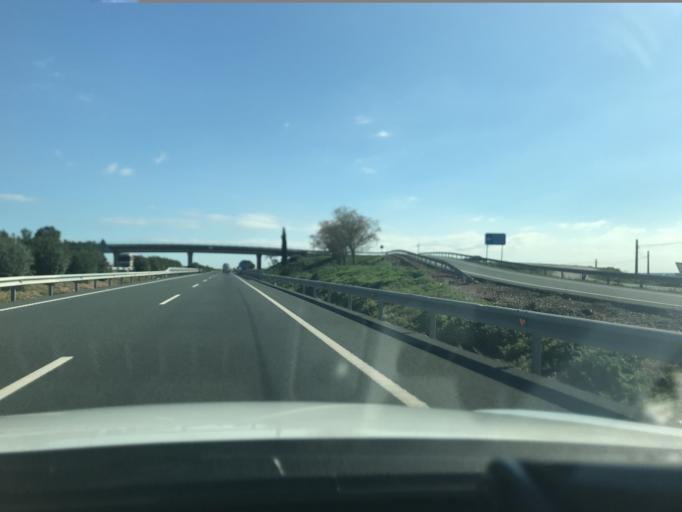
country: ES
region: Andalusia
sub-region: Provincia de Sevilla
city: La Luisiana
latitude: 37.5213
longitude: -5.3111
